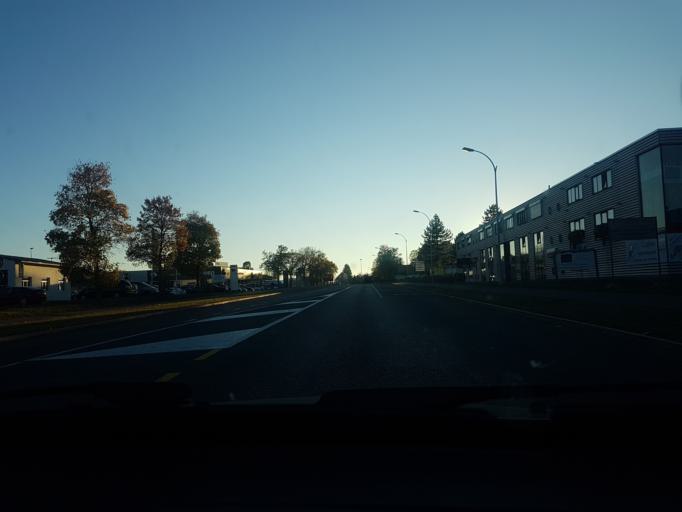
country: CH
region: Neuchatel
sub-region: La Chaux-de-Fonds District
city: La Chaux-de-Fonds
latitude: 47.0860
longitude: 6.8005
